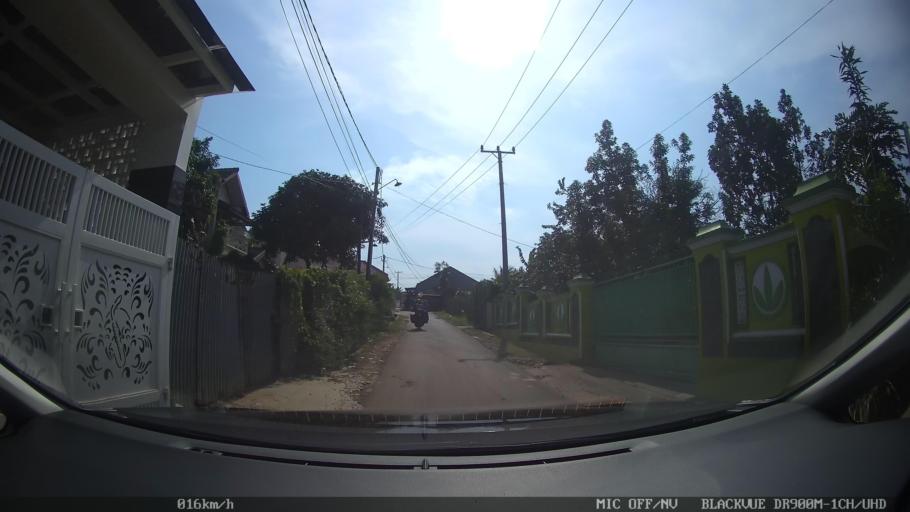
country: ID
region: Lampung
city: Kedaton
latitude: -5.3856
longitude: 105.2347
